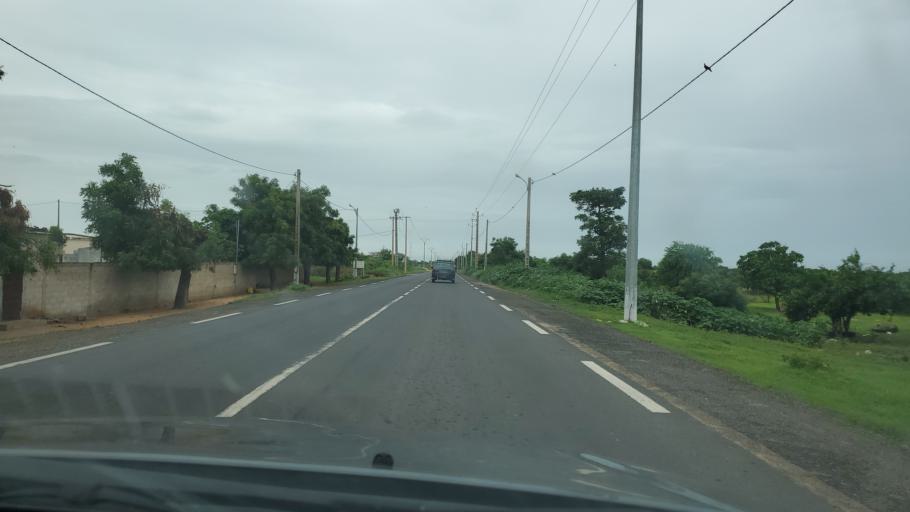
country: SN
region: Thies
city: Kayar
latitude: 15.0573
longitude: -16.9439
